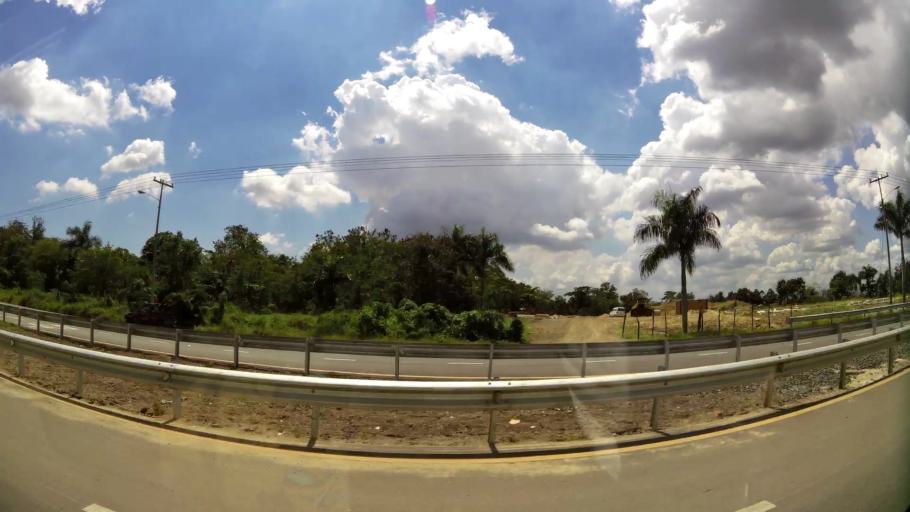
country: DO
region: Nacional
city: Santo Domingo
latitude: 18.5481
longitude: -69.9664
